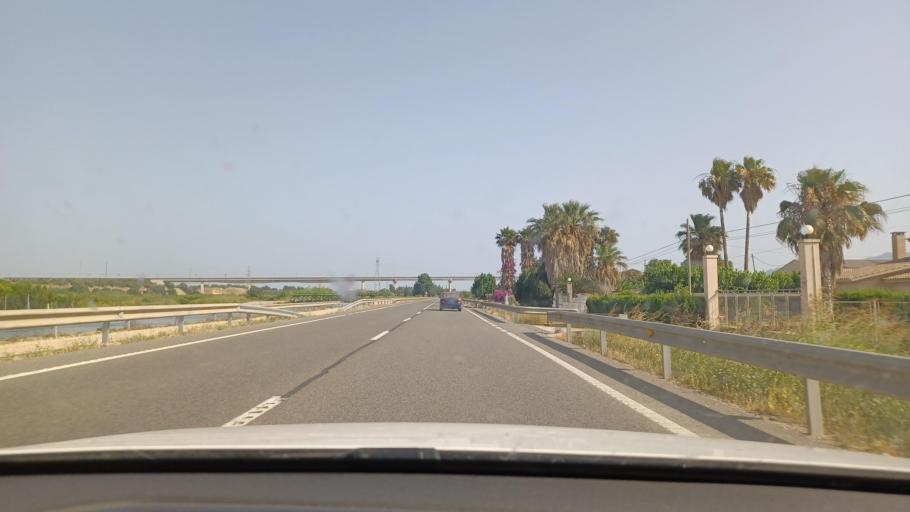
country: ES
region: Catalonia
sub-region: Provincia de Tarragona
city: Amposta
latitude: 40.7373
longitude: 0.5669
